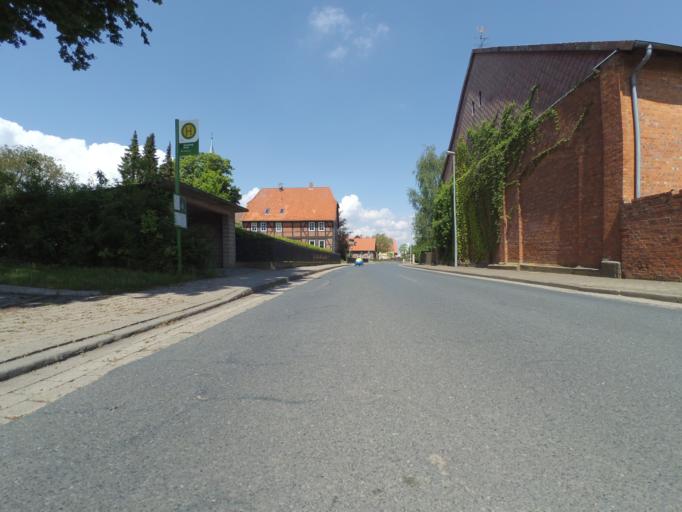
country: DE
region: Lower Saxony
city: Hohenhameln
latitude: 52.2198
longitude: 10.0344
